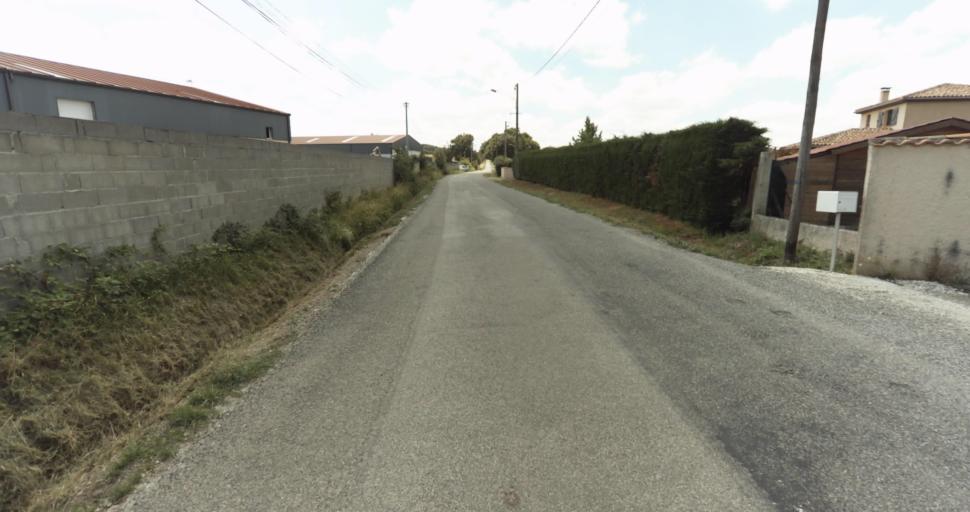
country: FR
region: Midi-Pyrenees
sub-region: Departement de la Haute-Garonne
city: Fontenilles
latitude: 43.5606
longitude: 1.1723
